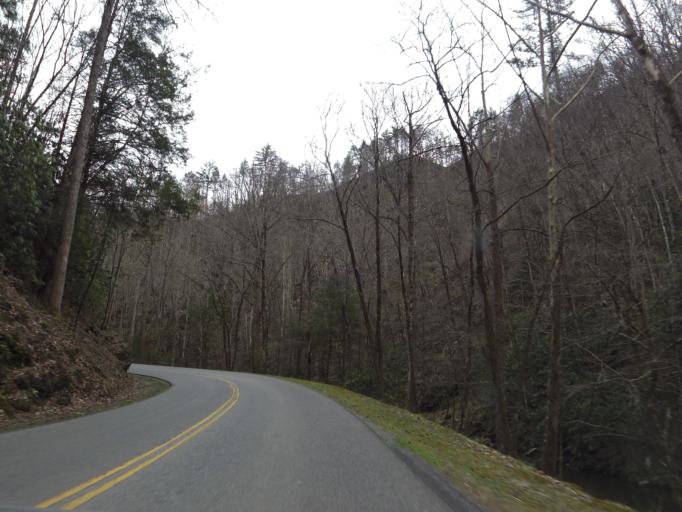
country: US
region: Tennessee
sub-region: Sevier County
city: Gatlinburg
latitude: 35.6446
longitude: -83.7167
